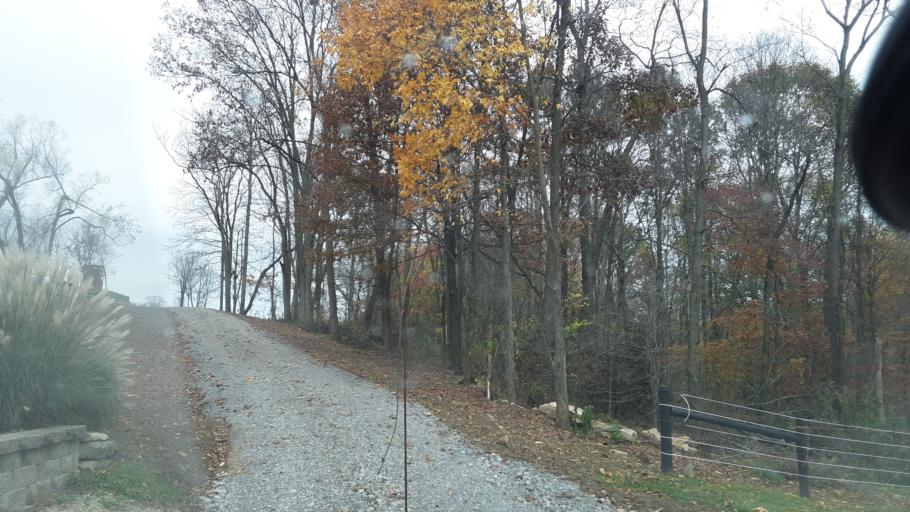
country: US
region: Ohio
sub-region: Holmes County
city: Millersburg
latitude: 40.4479
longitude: -81.8070
